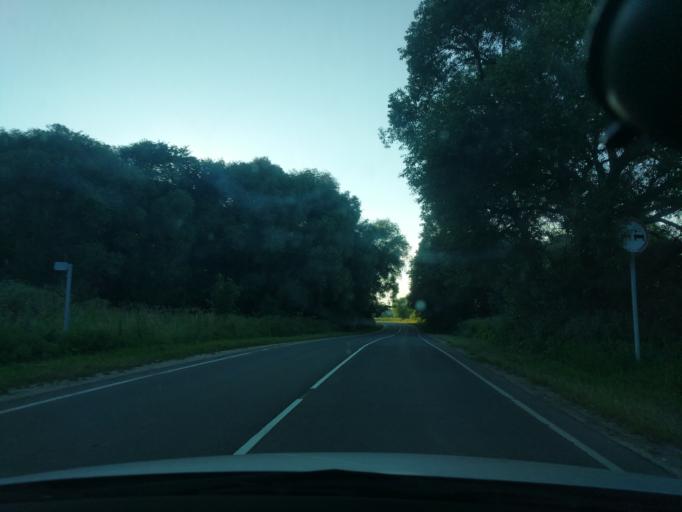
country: RU
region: Moskovskaya
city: Serpukhov
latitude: 54.8516
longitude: 37.4898
